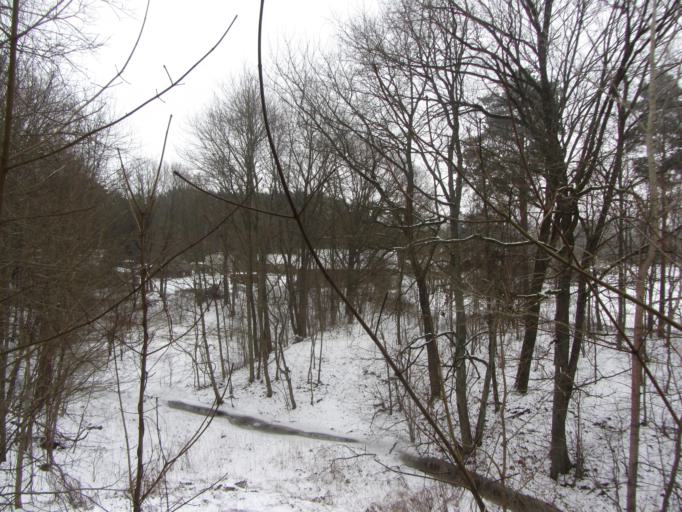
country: LT
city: Vilkija
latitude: 55.0380
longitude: 23.5329
